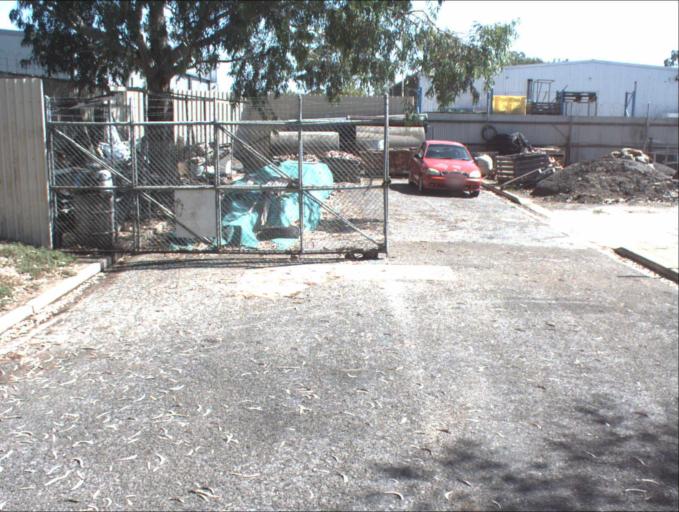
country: AU
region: South Australia
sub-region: Port Adelaide Enfield
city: Enfield
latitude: -34.8410
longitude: 138.5866
